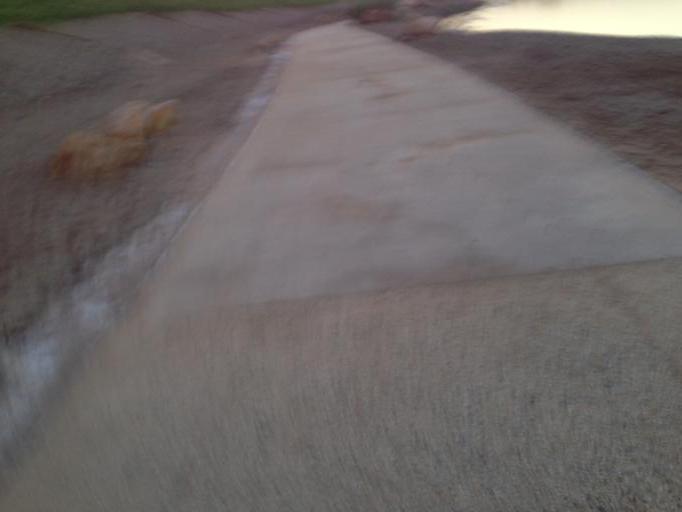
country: OM
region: Muhafazat Masqat
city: As Sib al Jadidah
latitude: 23.6224
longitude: 58.2698
